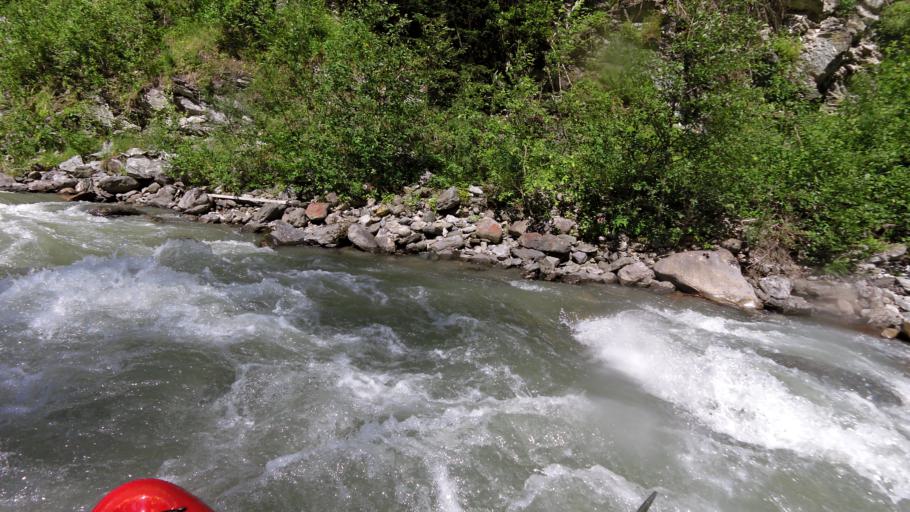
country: AT
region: Tyrol
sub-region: Politischer Bezirk Landeck
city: Strengen
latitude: 47.1245
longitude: 10.4621
